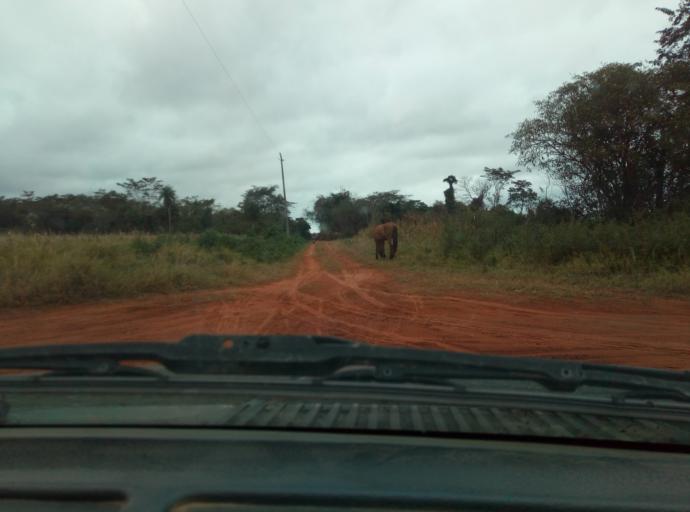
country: PY
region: Caaguazu
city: Doctor Cecilio Baez
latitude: -25.1614
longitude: -56.2720
